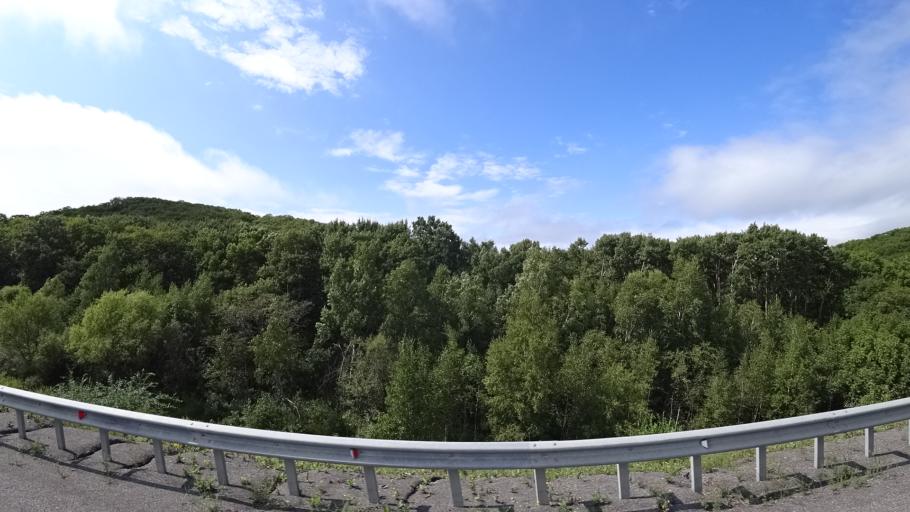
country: RU
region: Primorskiy
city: Lyalichi
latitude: 44.1253
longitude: 132.4236
